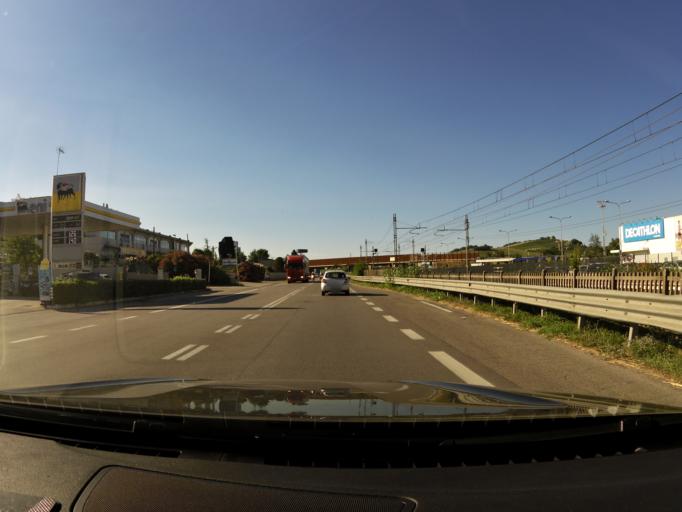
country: IT
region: The Marches
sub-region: Provincia di Ancona
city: San Biagio
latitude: 43.5228
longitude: 13.5233
